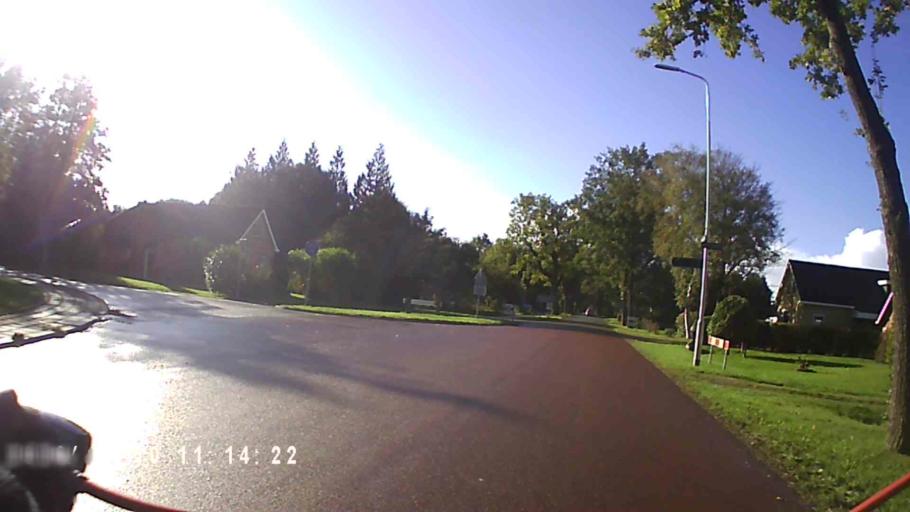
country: NL
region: Friesland
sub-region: Gemeente Smallingerland
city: Drachtstercompagnie
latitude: 53.1059
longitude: 6.2031
